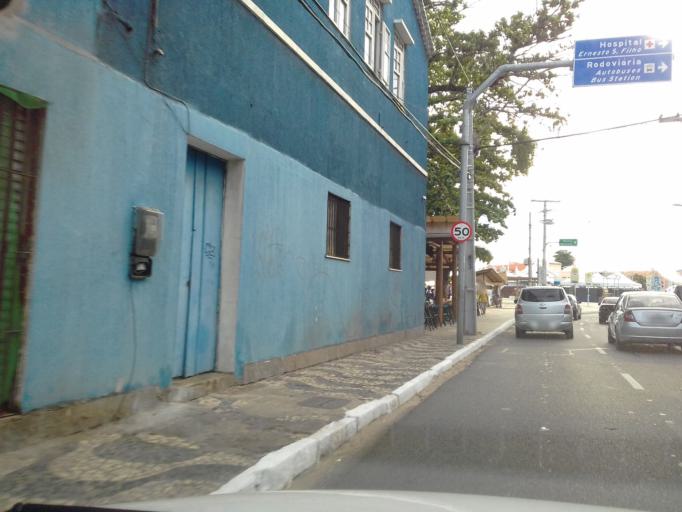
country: BR
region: Bahia
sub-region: Salvador
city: Salvador
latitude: -13.0131
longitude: -38.4882
